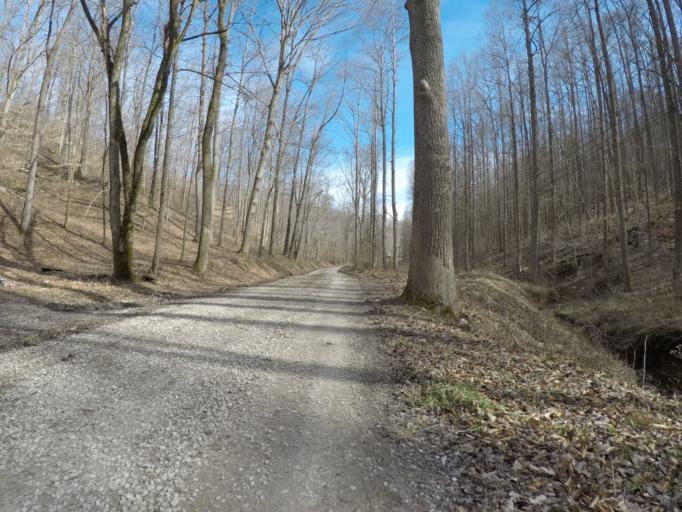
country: US
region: West Virginia
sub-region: Wayne County
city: Ceredo
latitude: 38.3445
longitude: -82.5451
